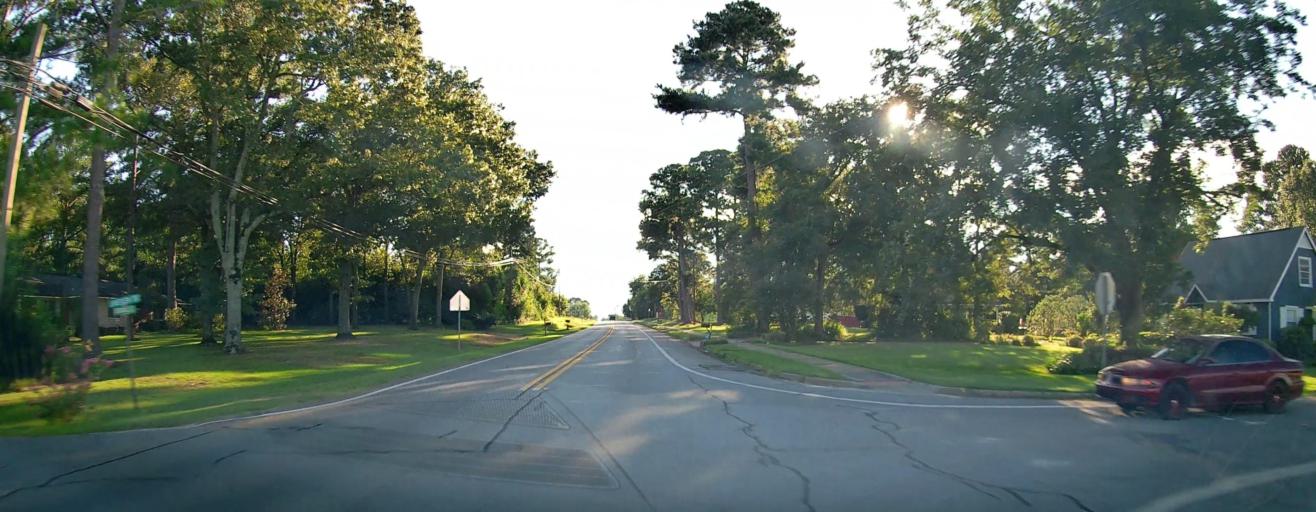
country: US
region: Georgia
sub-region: Pulaski County
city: Hawkinsville
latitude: 32.2809
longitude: -83.4846
